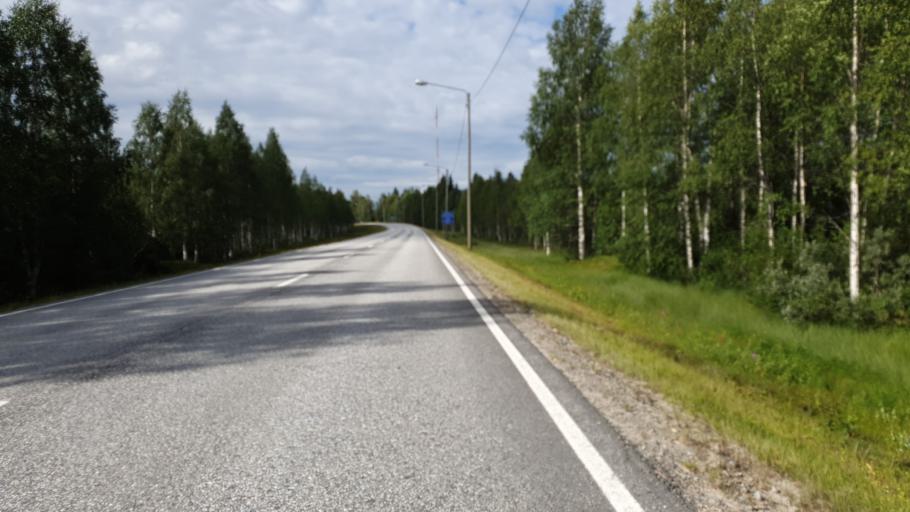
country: FI
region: Kainuu
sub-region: Kehys-Kainuu
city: Kuhmo
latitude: 64.5408
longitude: 29.9554
